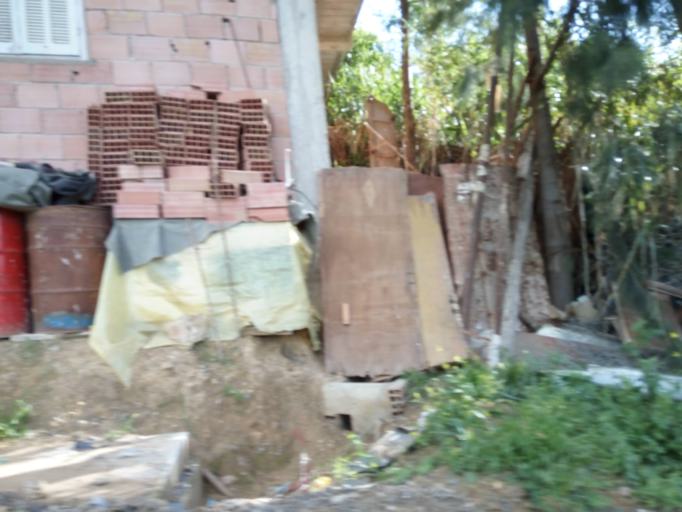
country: DZ
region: Tipaza
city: El Affroun
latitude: 36.3733
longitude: 2.4982
